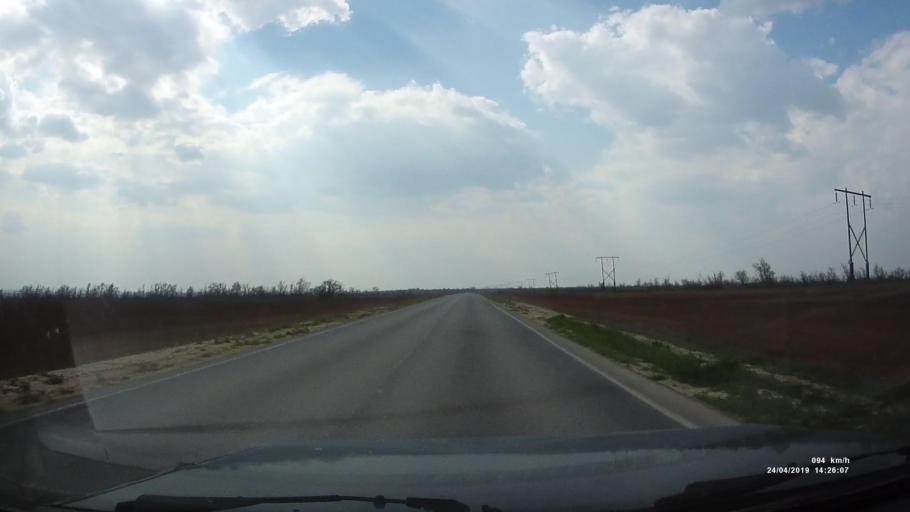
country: RU
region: Kalmykiya
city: Arshan'
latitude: 46.3328
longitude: 44.0686
